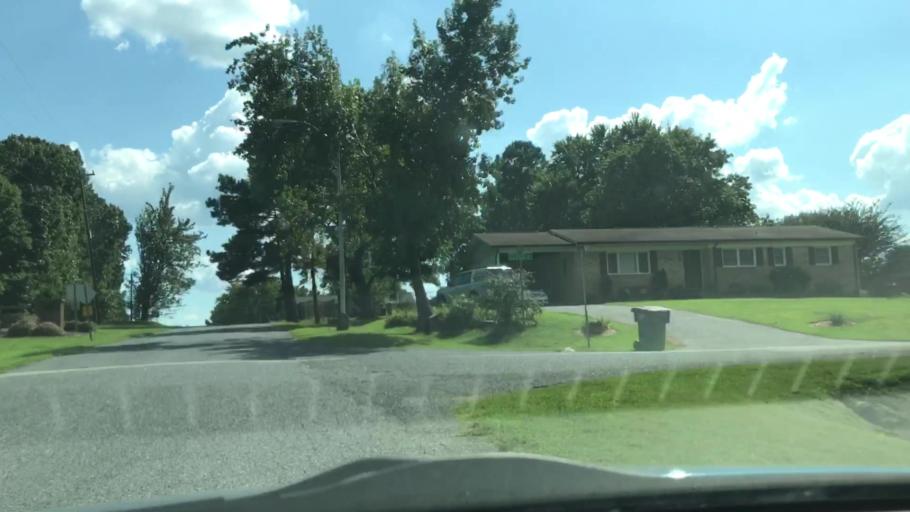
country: US
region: North Carolina
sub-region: Randolph County
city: Asheboro
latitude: 35.7509
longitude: -79.8140
